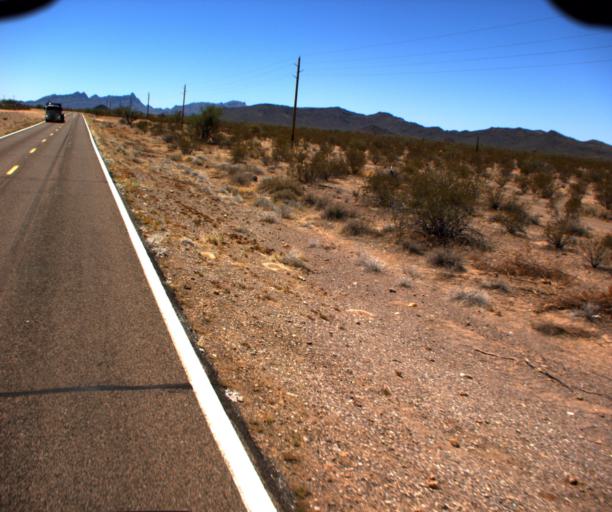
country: US
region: Arizona
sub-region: Pima County
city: Ajo
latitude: 32.2488
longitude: -112.7299
